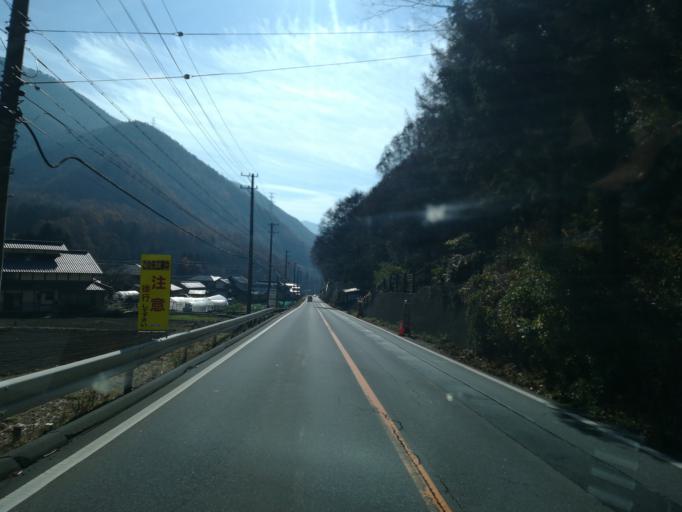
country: JP
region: Nagano
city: Ueda
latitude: 36.4762
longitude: 138.3453
